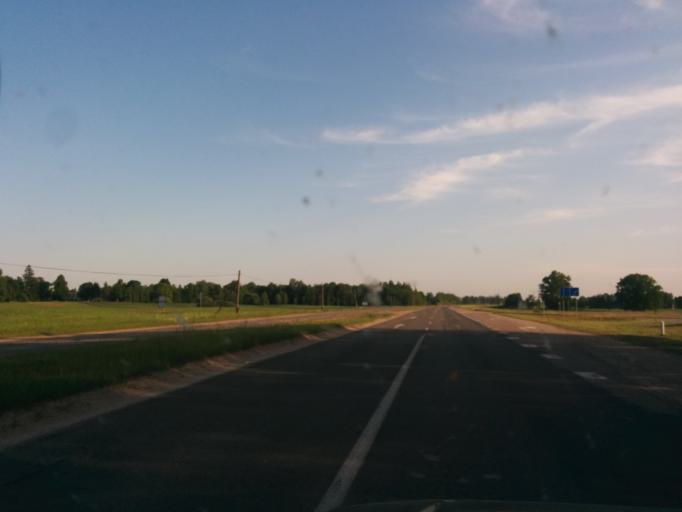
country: LV
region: Talsu Rajons
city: Talsi
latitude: 57.2289
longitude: 22.5845
